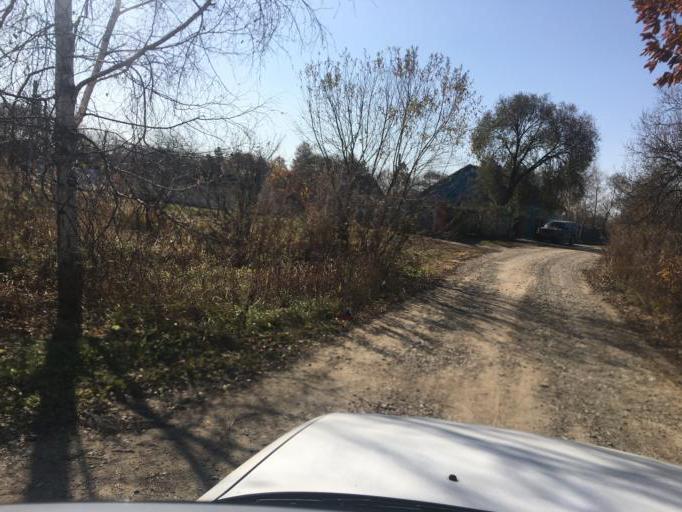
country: RU
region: Primorskiy
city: Dal'nerechensk
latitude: 45.9174
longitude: 133.7882
